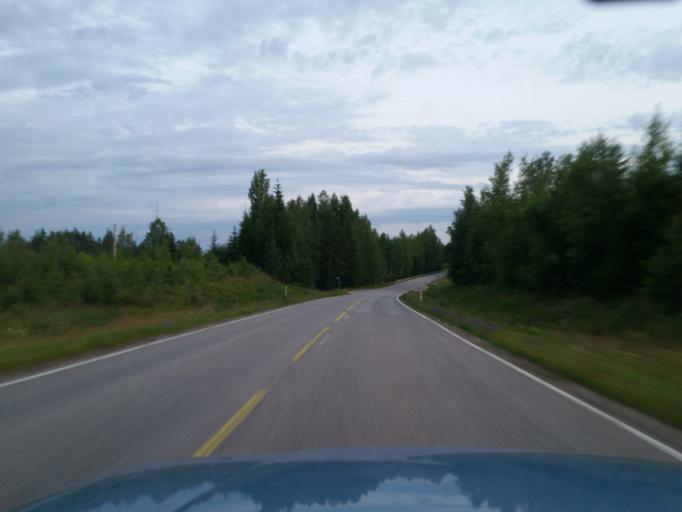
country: FI
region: Southern Savonia
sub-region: Savonlinna
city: Sulkava
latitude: 61.8244
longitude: 28.4399
